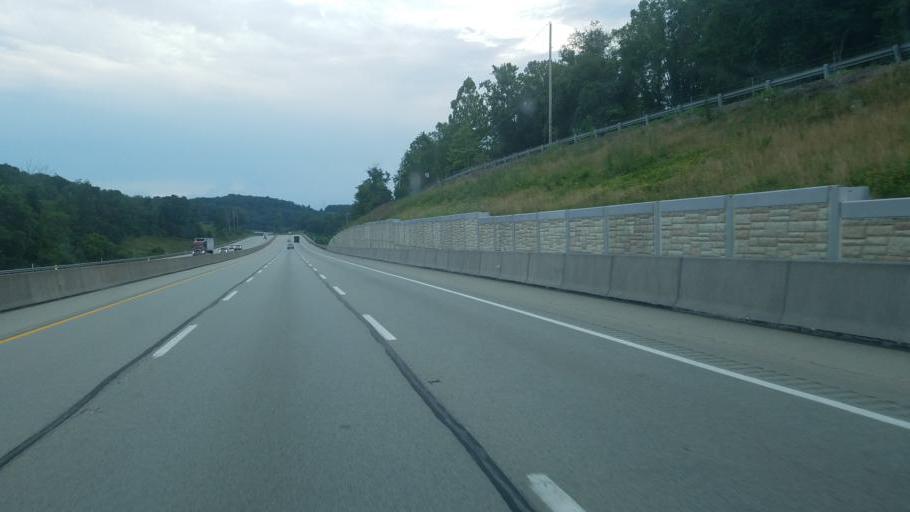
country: US
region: Pennsylvania
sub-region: Westmoreland County
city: Manor
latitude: 40.2775
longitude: -79.6688
